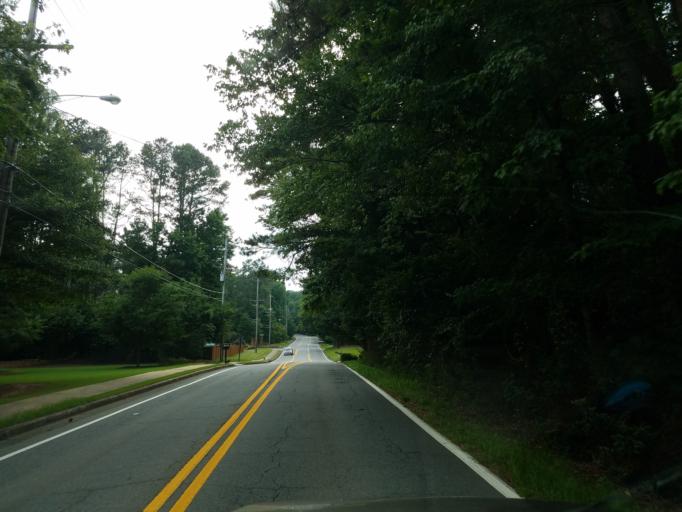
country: US
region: Georgia
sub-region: Cobb County
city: Marietta
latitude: 33.9749
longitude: -84.4929
